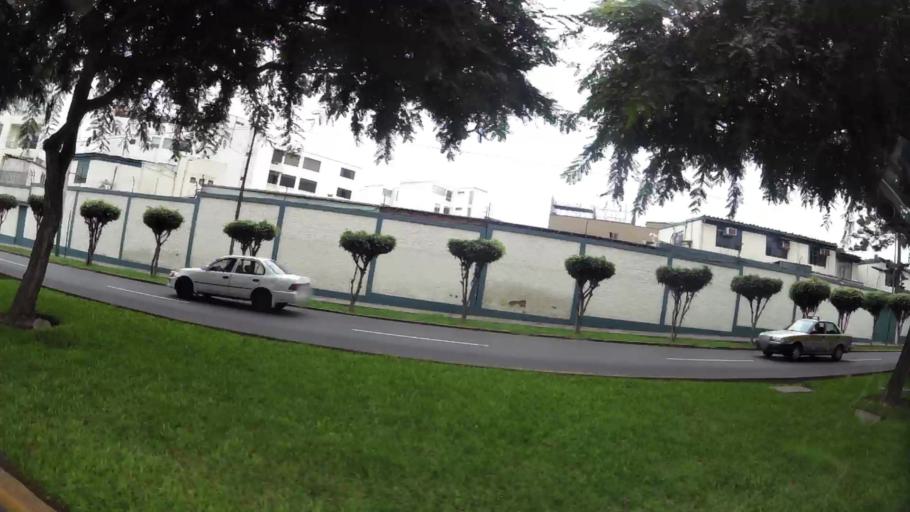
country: PE
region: Lima
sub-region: Lima
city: Surco
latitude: -12.1212
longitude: -76.9887
